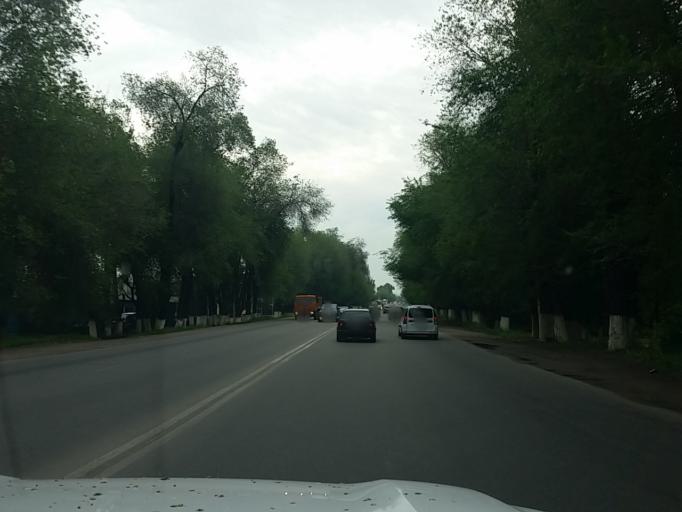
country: KZ
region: Almaty Oblysy
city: Energeticheskiy
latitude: 43.3399
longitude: 77.0440
